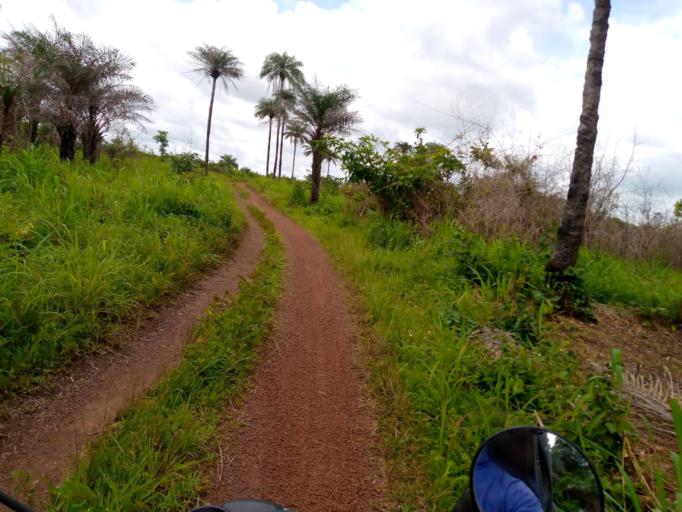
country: SL
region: Northern Province
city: Mange
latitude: 8.9911
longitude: -12.7717
